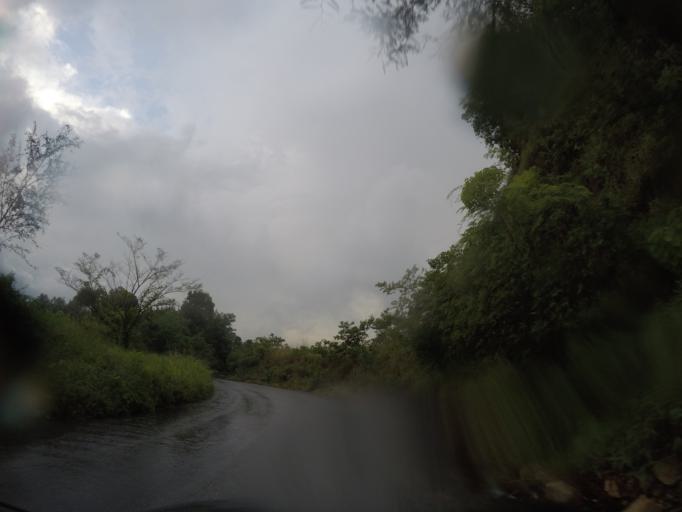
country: MX
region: Oaxaca
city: San Gabriel Mixtepec
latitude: 16.0590
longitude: -97.0750
